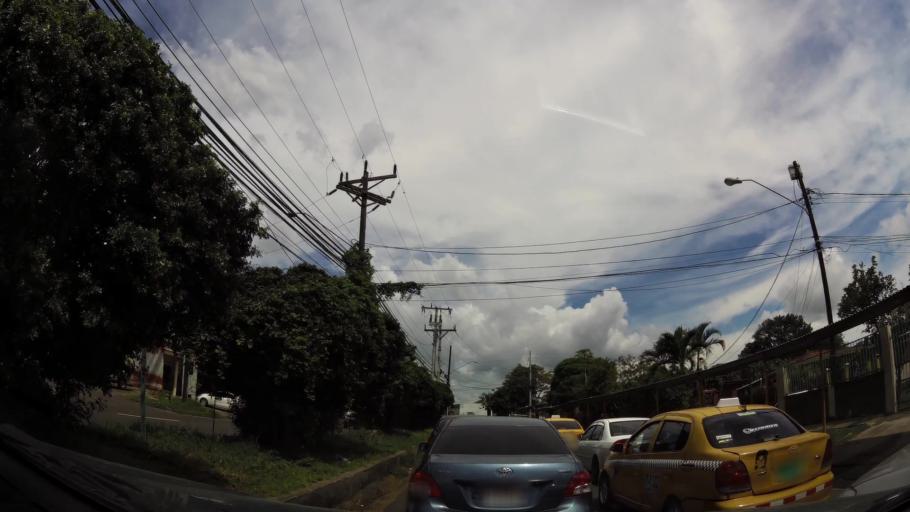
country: PA
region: Panama
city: San Vicente de Bique
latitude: 8.9199
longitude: -79.6966
